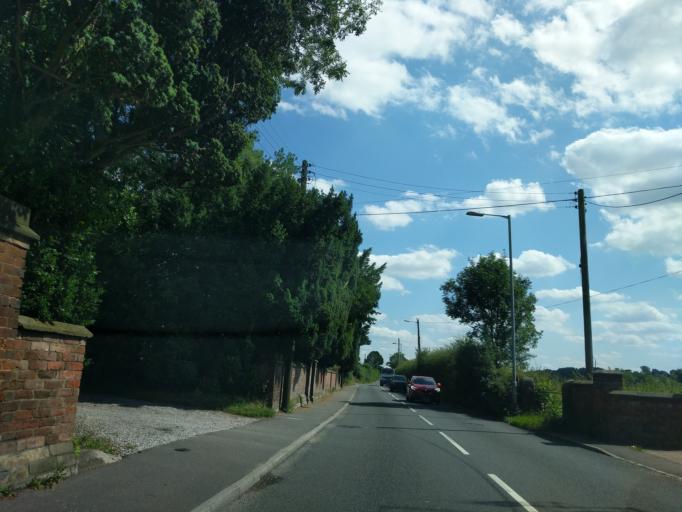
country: GB
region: England
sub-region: Staffordshire
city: Cheadle
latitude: 52.9515
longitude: -1.9846
